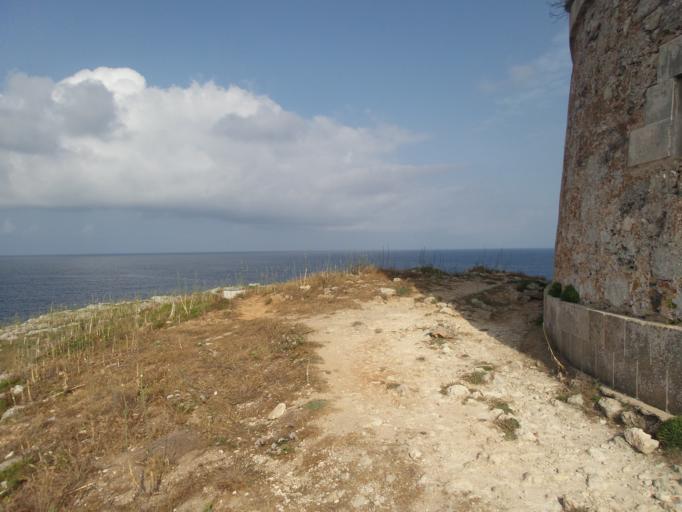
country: ES
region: Balearic Islands
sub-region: Illes Balears
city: Sant Lluis
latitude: 39.8252
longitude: 4.2960
